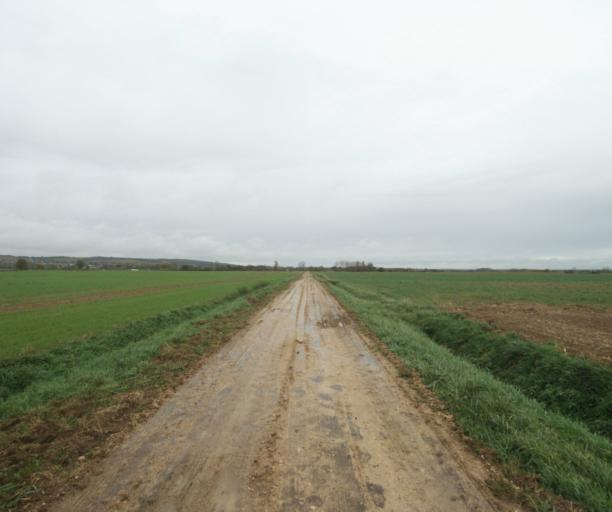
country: FR
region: Rhone-Alpes
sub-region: Departement de l'Ain
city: Pont-de-Vaux
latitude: 46.4787
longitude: 4.8917
